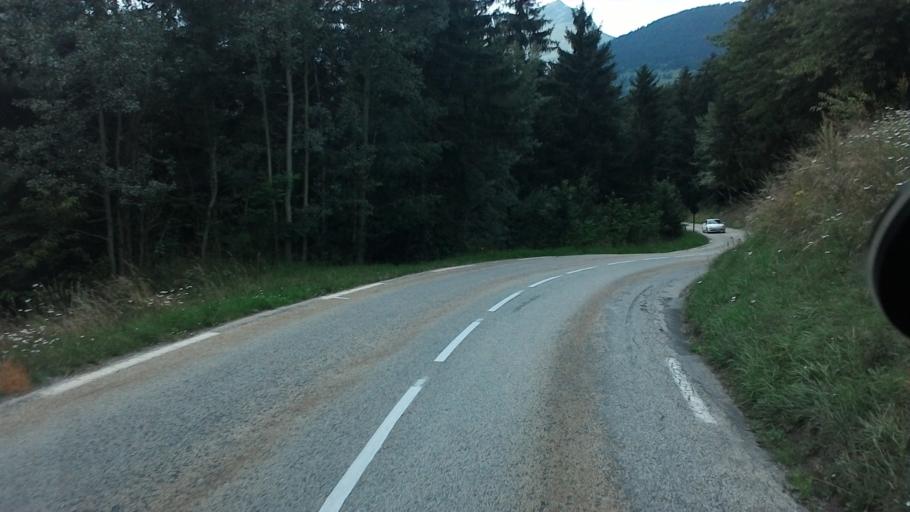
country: FR
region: Rhone-Alpes
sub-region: Departement de la Savoie
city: Seez
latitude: 45.6212
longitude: 6.8233
